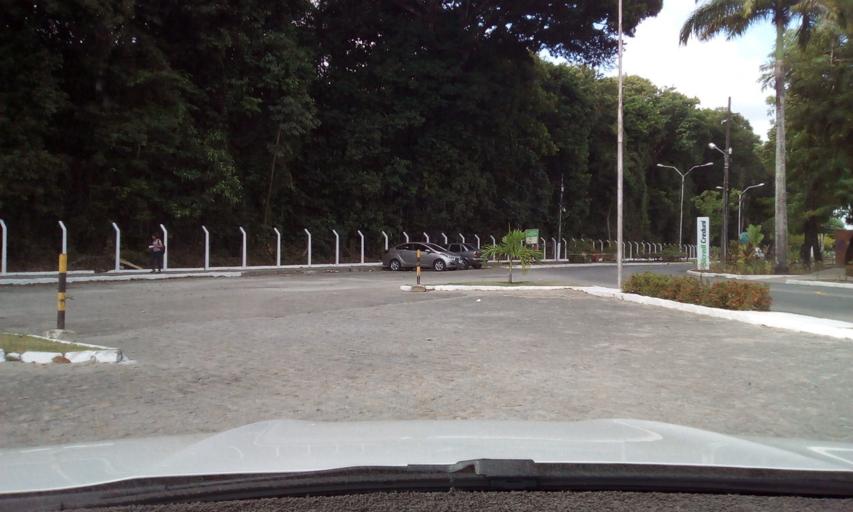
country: BR
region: Paraiba
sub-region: Joao Pessoa
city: Joao Pessoa
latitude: -7.1378
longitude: -34.8475
